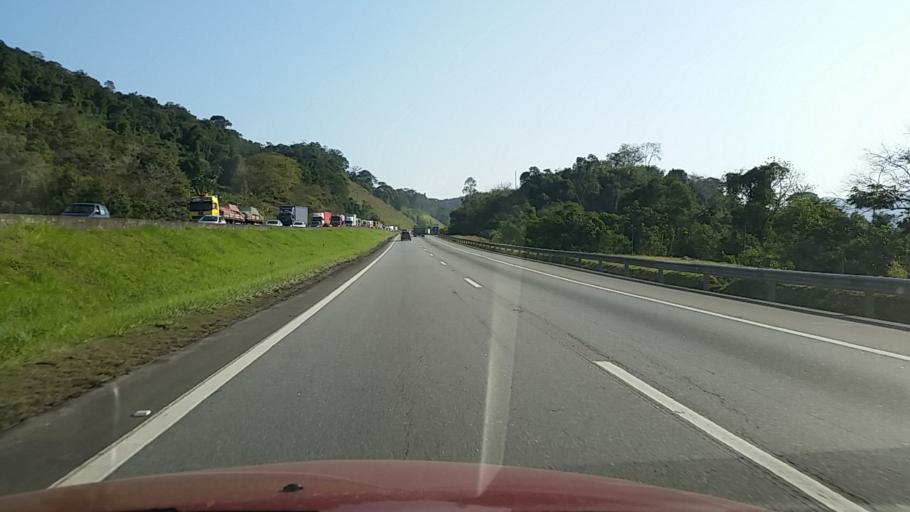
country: BR
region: Sao Paulo
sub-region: Miracatu
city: Miracatu
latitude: -24.1788
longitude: -47.3496
